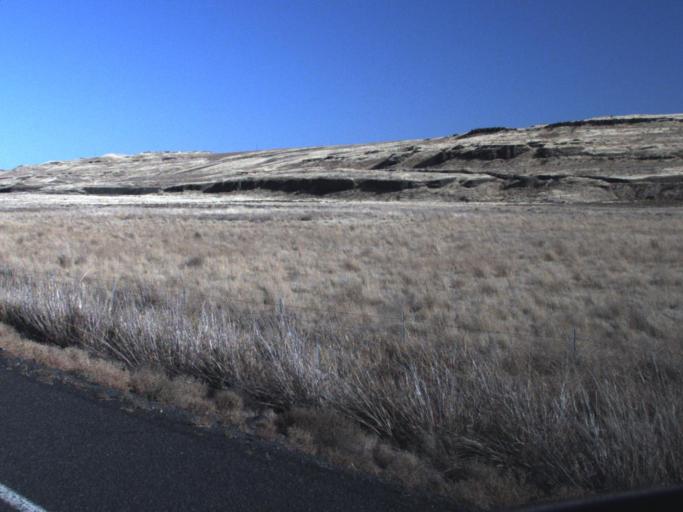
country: US
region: Washington
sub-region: Adams County
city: Ritzville
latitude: 46.7236
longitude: -118.3685
